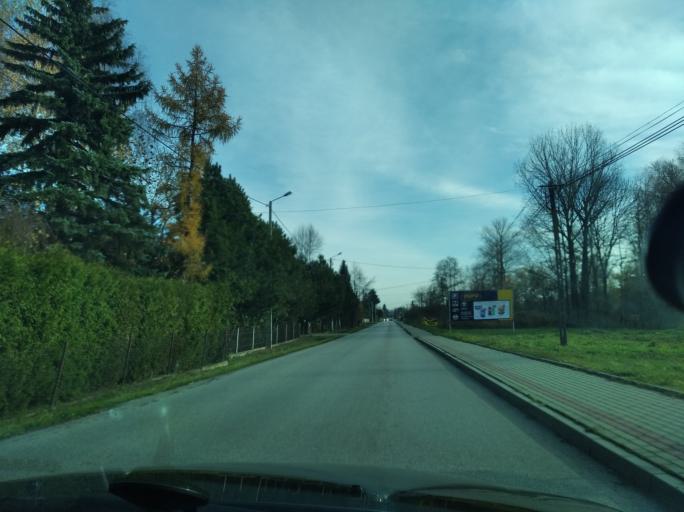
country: PL
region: Subcarpathian Voivodeship
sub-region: Powiat lancucki
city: Kraczkowa
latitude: 50.0380
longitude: 22.1559
